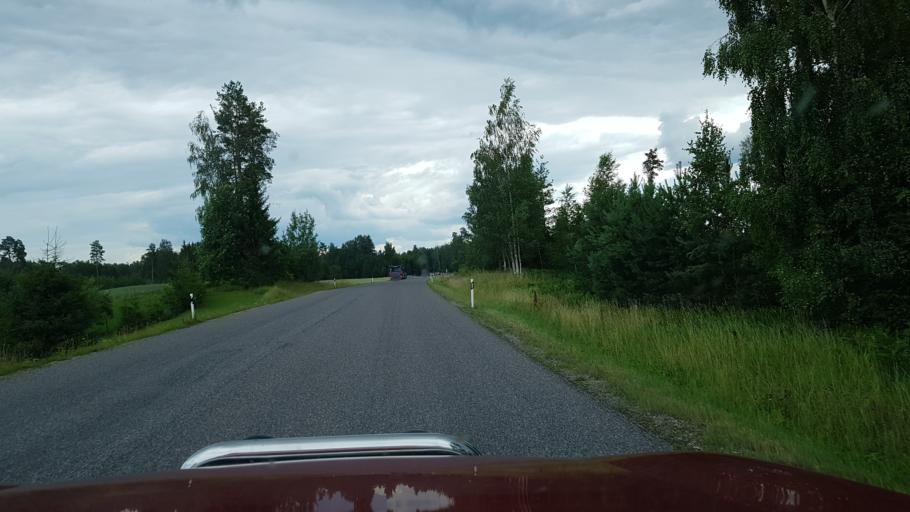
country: EE
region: Polvamaa
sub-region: Polva linn
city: Polva
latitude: 58.1455
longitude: 27.2338
